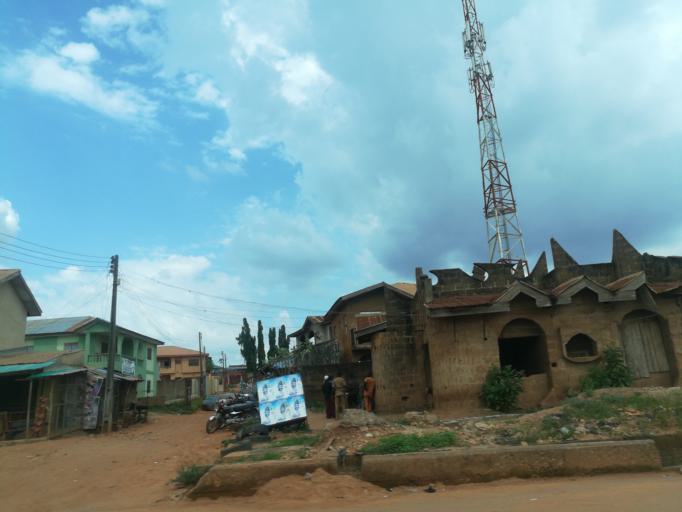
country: NG
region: Oyo
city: Ido
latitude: 7.4331
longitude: 3.8347
